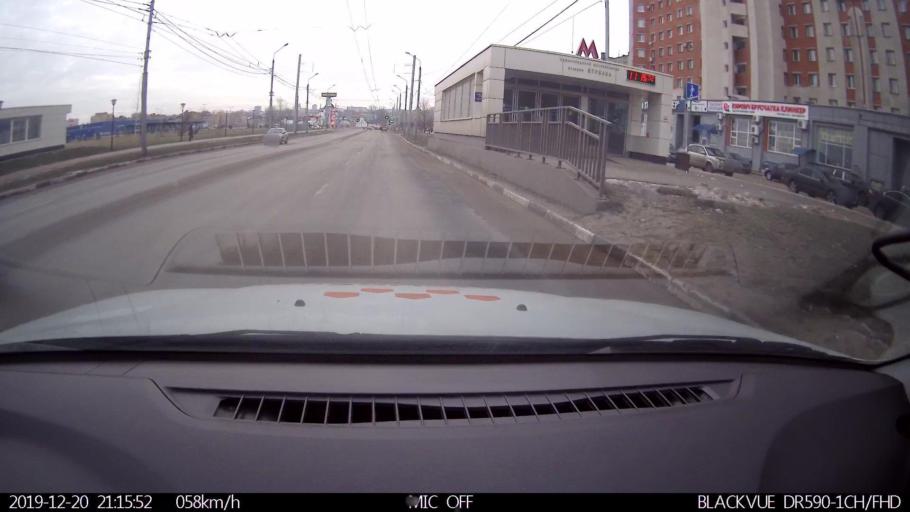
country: RU
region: Nizjnij Novgorod
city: Nizhniy Novgorod
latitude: 56.3344
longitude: 43.9453
